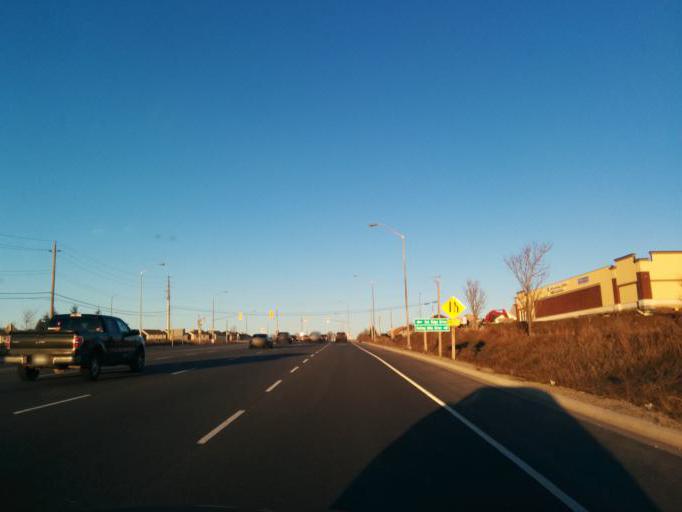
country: CA
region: Ontario
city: Orangeville
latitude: 43.9211
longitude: -80.0750
